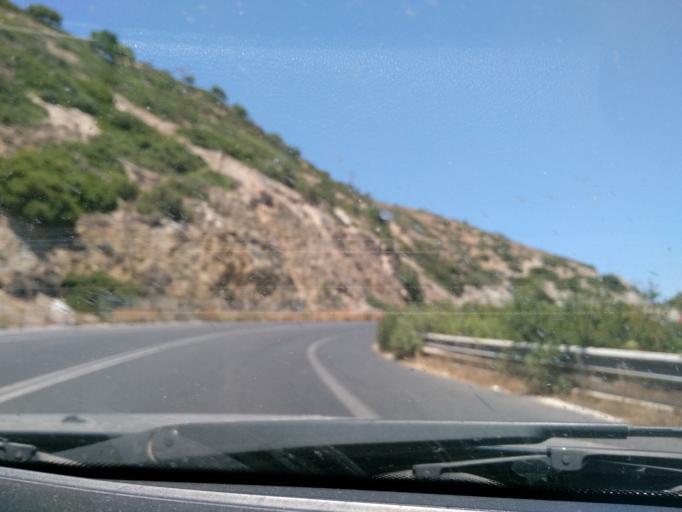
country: GR
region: Crete
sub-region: Nomos Irakleiou
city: Gazi
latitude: 35.3829
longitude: 25.0357
